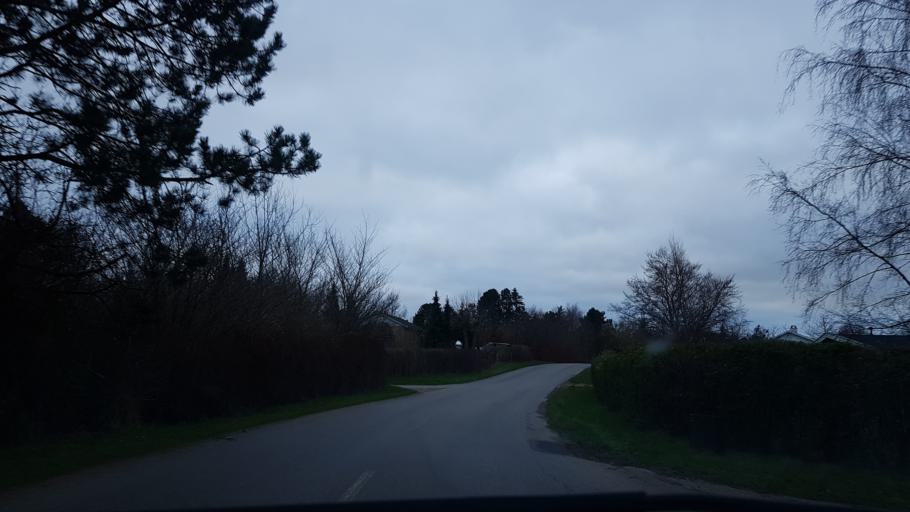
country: DK
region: Zealand
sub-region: Odsherred Kommune
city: Hojby
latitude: 55.9393
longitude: 11.6113
